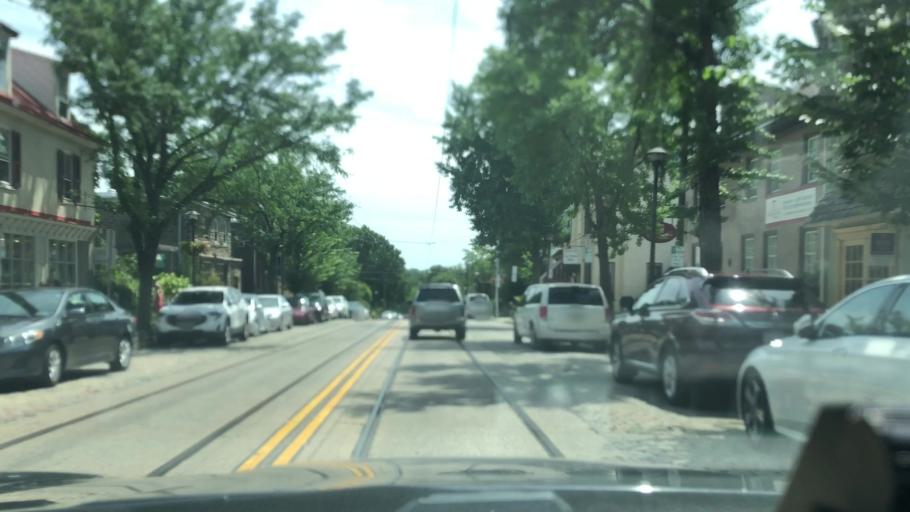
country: US
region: Pennsylvania
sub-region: Montgomery County
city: Wyndmoor
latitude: 40.0730
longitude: -75.2027
